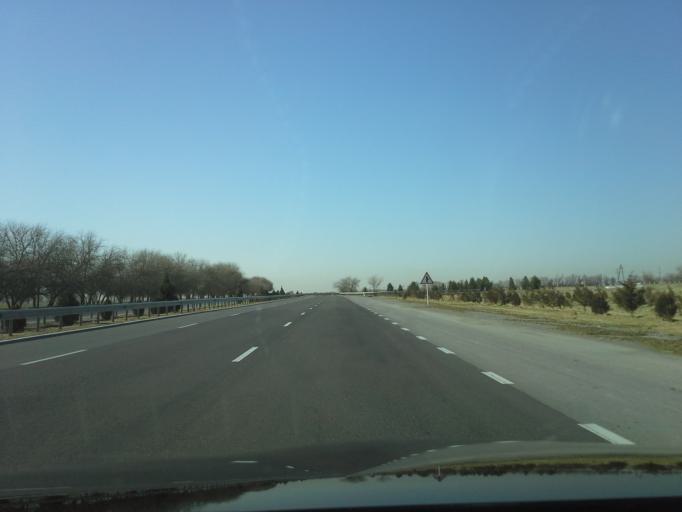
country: TM
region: Ahal
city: Annau
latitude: 37.9007
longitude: 58.5752
